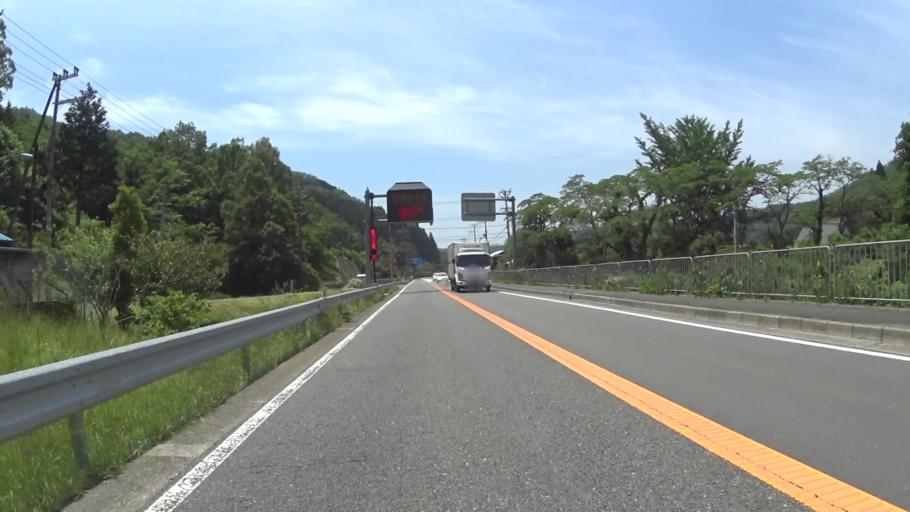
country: JP
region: Kyoto
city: Ayabe
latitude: 35.2083
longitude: 135.2796
